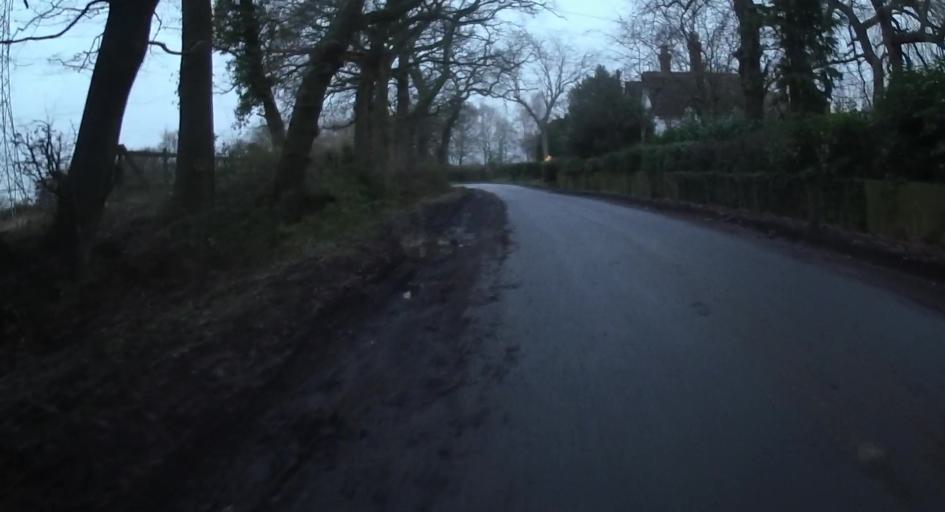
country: GB
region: England
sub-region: Hampshire
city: Tadley
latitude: 51.3295
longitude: -1.0880
